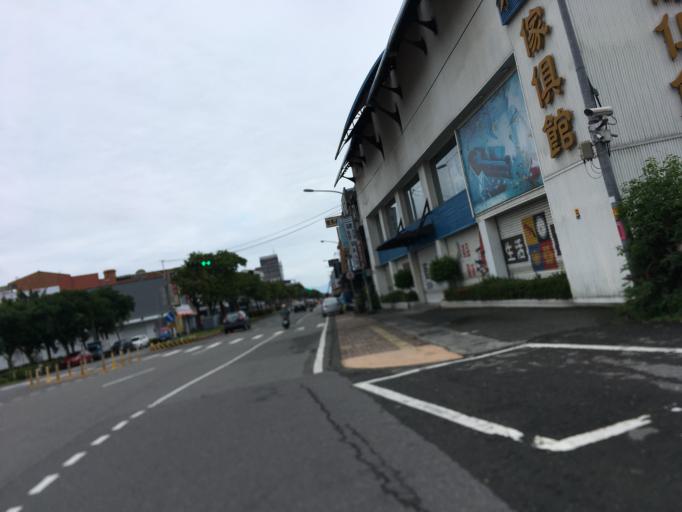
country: TW
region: Taiwan
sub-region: Yilan
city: Yilan
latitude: 24.6989
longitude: 121.7689
